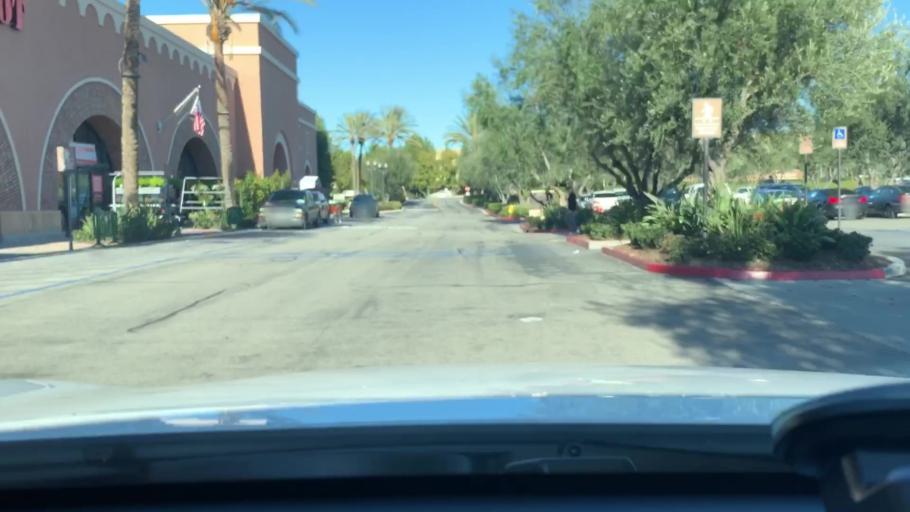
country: US
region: California
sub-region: Orange County
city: Lake Forest
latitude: 33.6992
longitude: -117.7416
